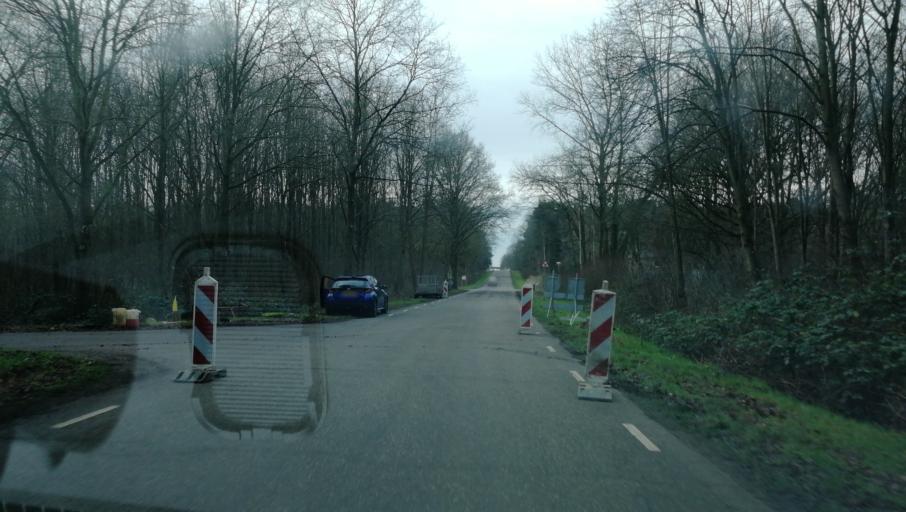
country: NL
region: Limburg
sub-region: Gemeente Venlo
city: Venlo
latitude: 51.3962
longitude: 6.1889
